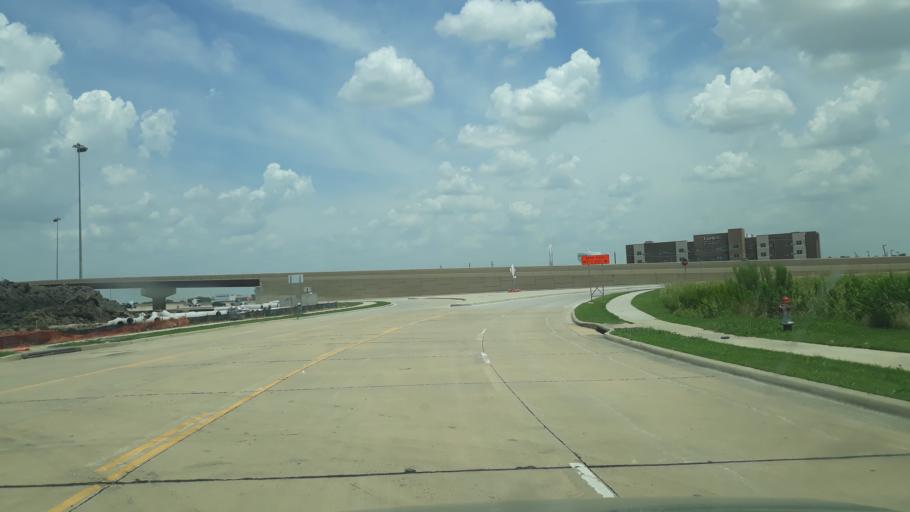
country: US
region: Texas
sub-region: Dallas County
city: Coppell
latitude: 32.9699
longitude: -97.0336
